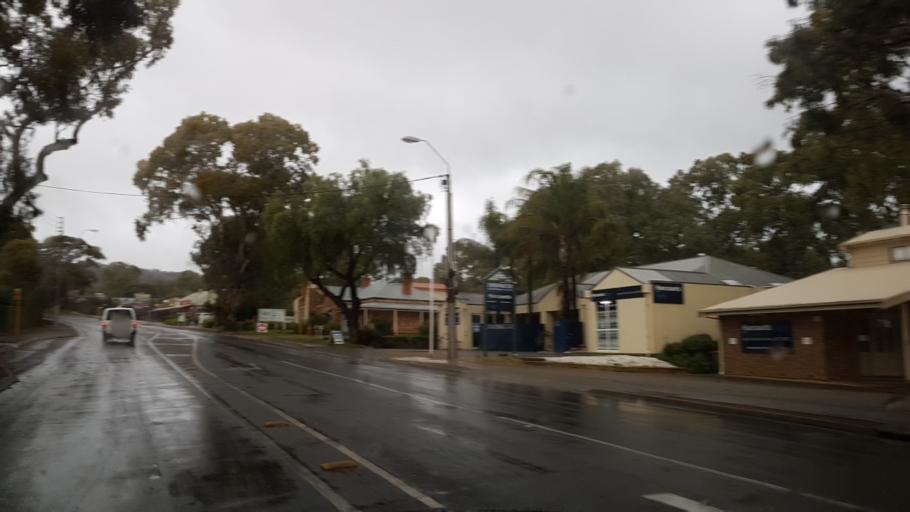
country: AU
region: South Australia
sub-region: Marion
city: Trott Park
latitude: -35.0856
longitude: 138.5863
